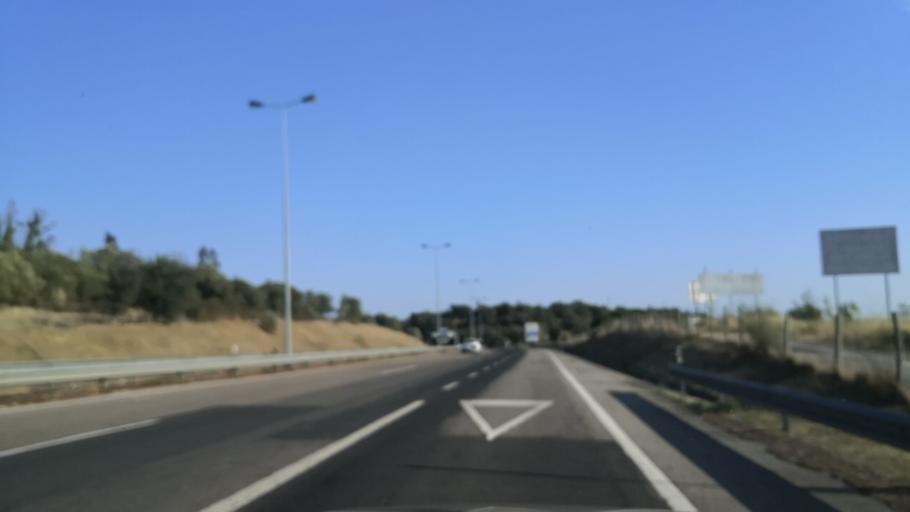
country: PT
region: Santarem
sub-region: Santarem
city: Santarem
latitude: 39.2293
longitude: -8.7048
